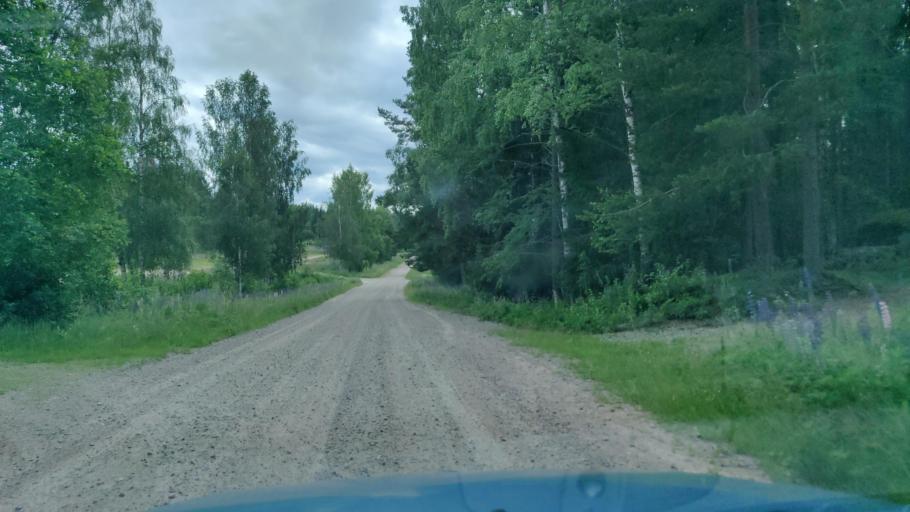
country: SE
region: Vaermland
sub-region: Hagfors Kommun
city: Hagfors
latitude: 60.0321
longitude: 13.7145
